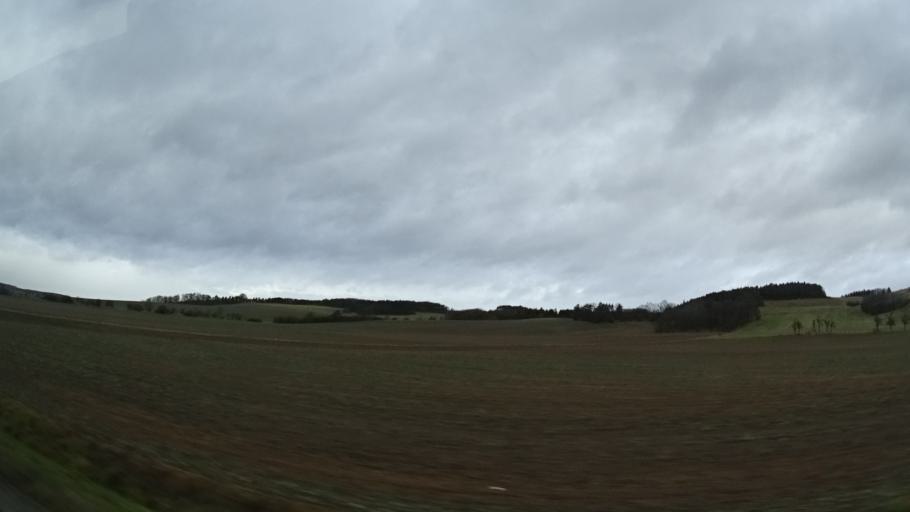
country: DE
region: Thuringia
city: Blankenhain
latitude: 50.8540
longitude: 11.3876
